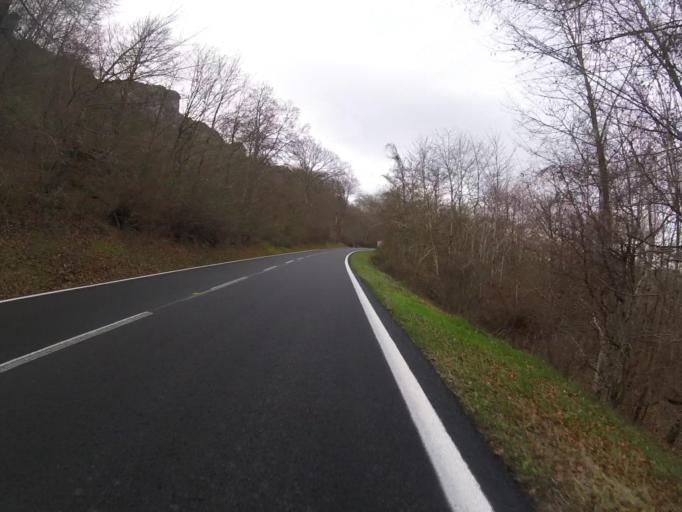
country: ES
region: Navarre
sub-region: Provincia de Navarra
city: Arbizu
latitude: 42.8658
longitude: -2.0211
